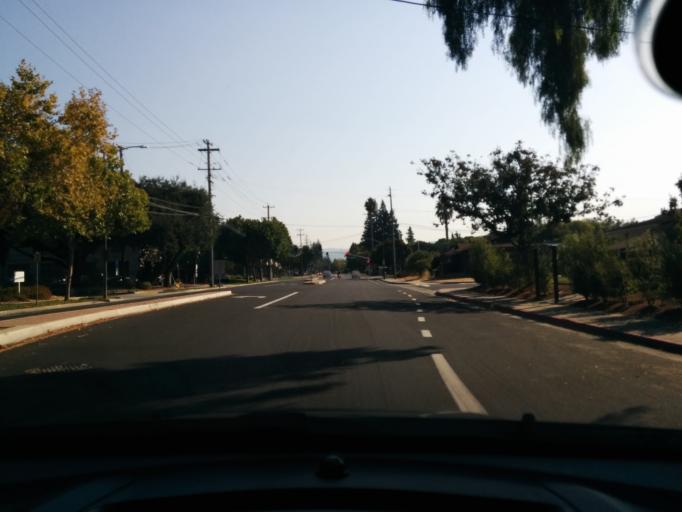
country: US
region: California
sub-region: Santa Clara County
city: Mountain View
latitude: 37.3985
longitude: -122.0592
